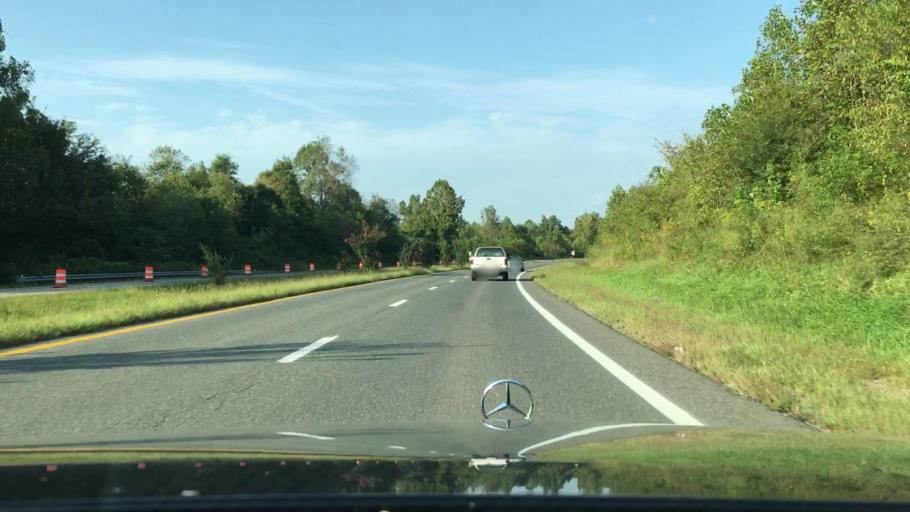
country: US
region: Virginia
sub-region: Amherst County
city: Madison Heights
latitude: 37.5206
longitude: -79.1168
